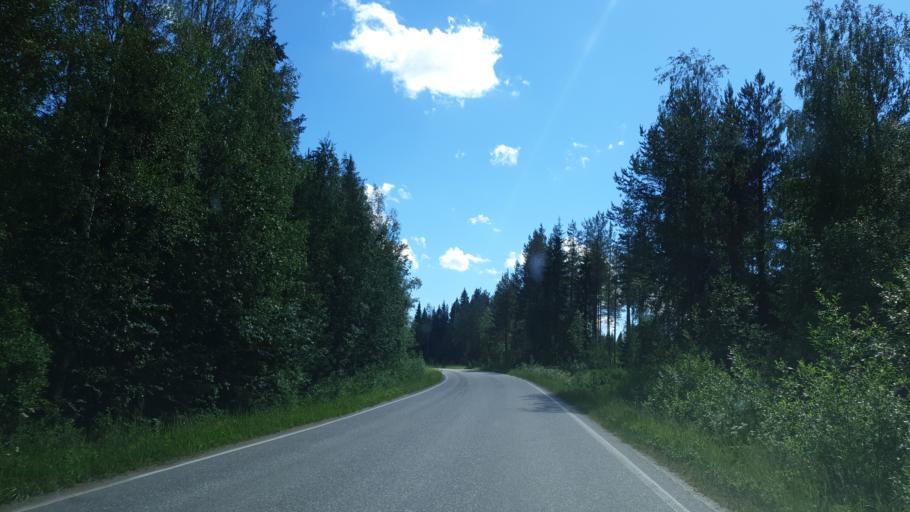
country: FI
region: Northern Savo
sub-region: Koillis-Savo
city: Kaavi
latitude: 63.0016
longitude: 28.5019
